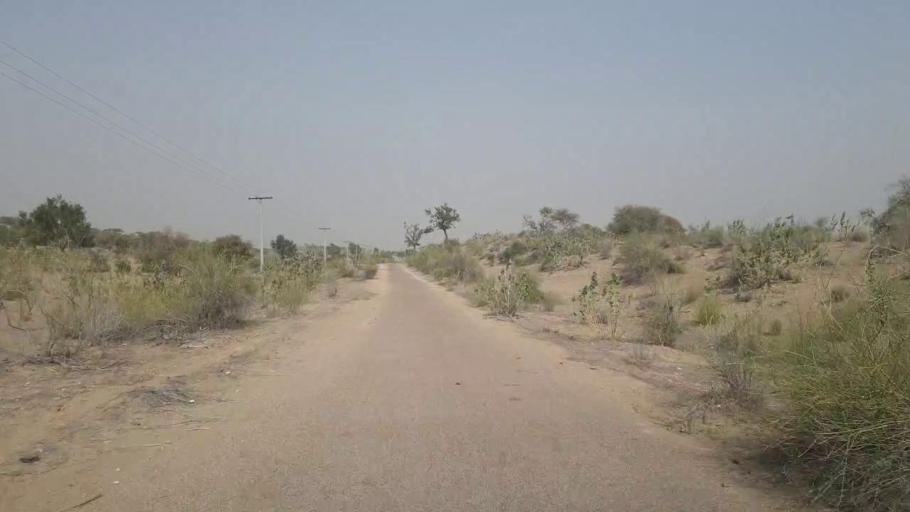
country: PK
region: Sindh
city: Chor
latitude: 25.6247
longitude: 70.0273
